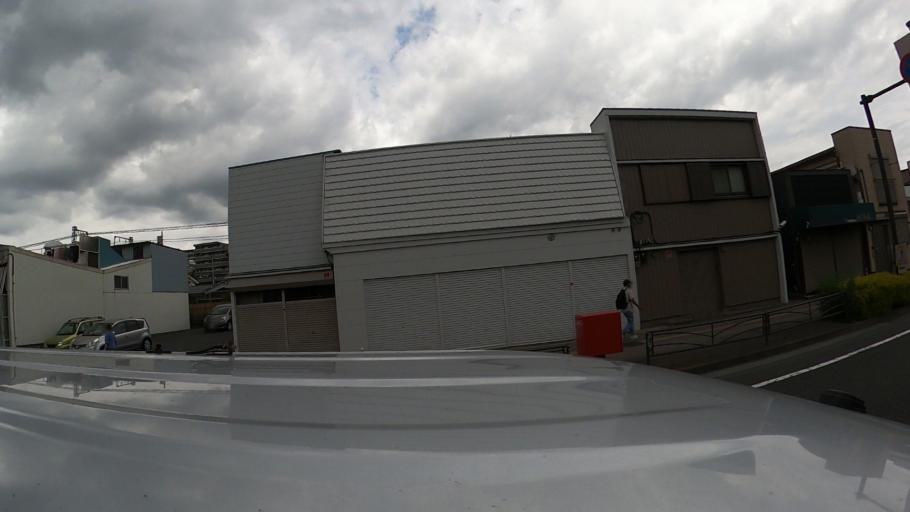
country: JP
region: Kanagawa
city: Yokohama
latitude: 35.4883
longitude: 139.6586
